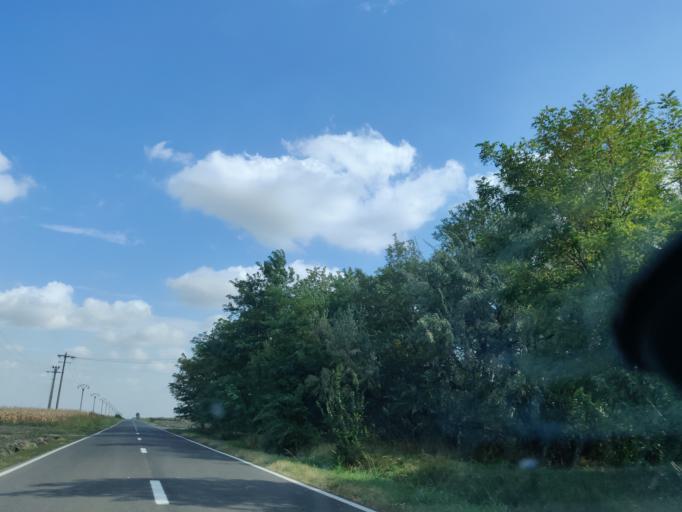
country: RO
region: Vrancea
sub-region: Comuna Maicanesti
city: Ramniceni
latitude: 45.4579
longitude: 27.4091
